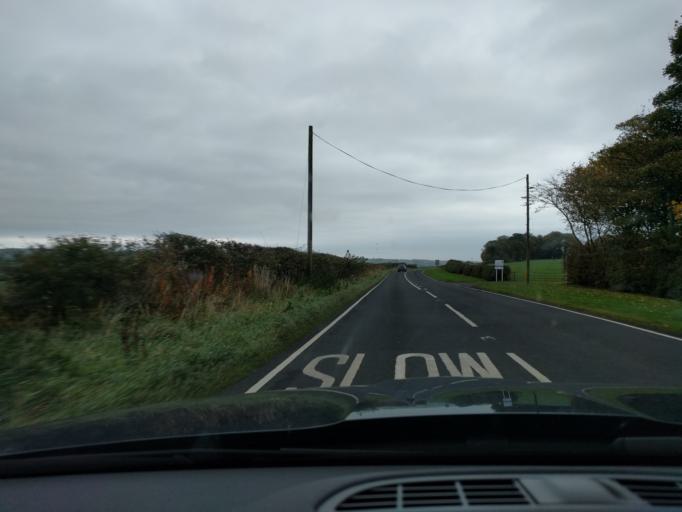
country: GB
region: England
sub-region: Northumberland
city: Berwick-Upon-Tweed
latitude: 55.7457
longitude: -2.0718
